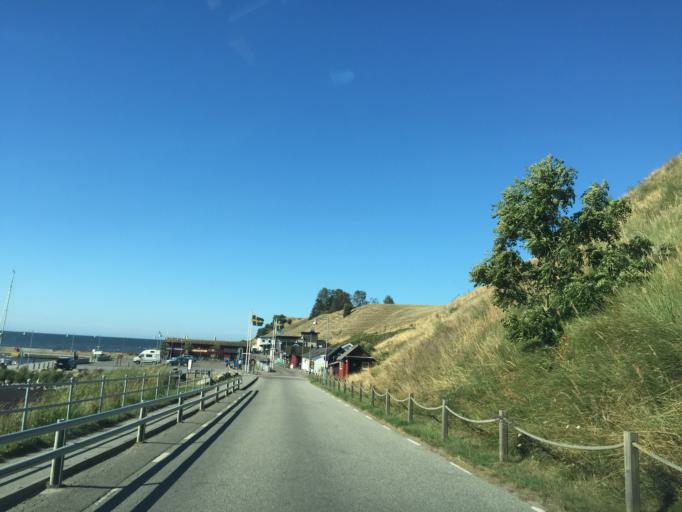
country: SE
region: Skane
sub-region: Ystads Kommun
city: Kopingebro
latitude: 55.3843
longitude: 14.0645
